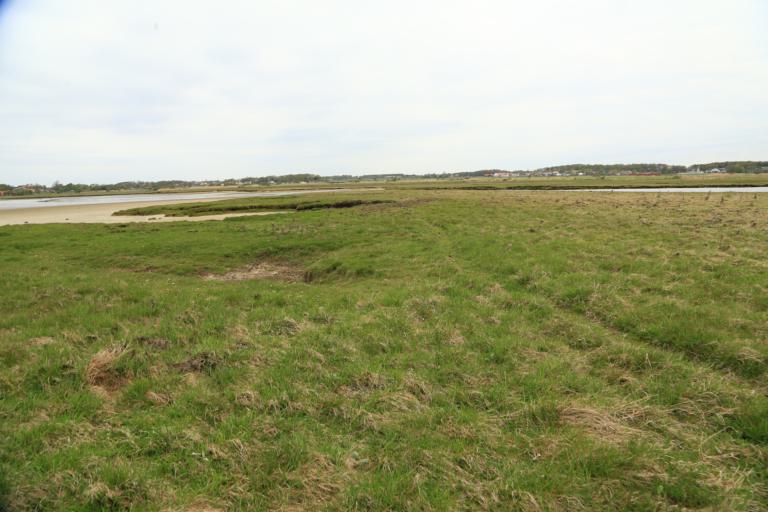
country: SE
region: Halland
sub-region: Varbergs Kommun
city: Traslovslage
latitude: 57.0323
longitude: 12.3169
